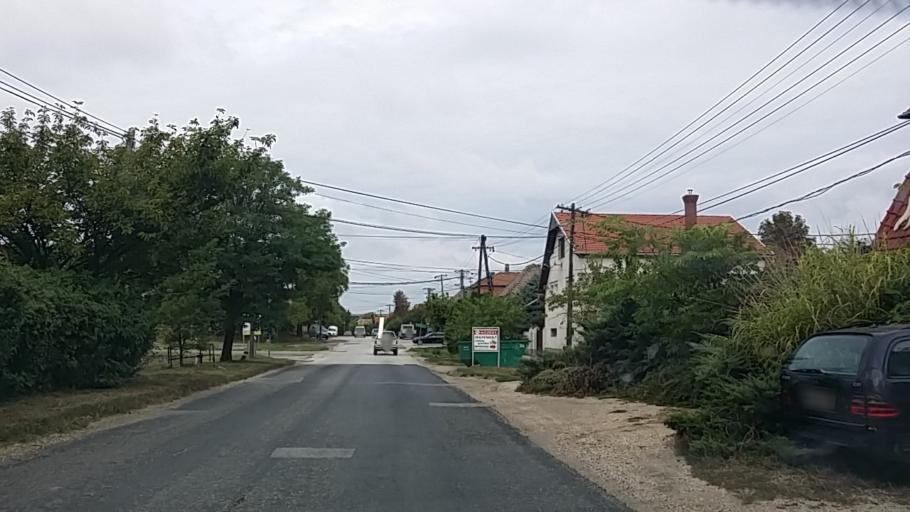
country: HU
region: Komarom-Esztergom
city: Tata
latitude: 47.6458
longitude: 18.3072
